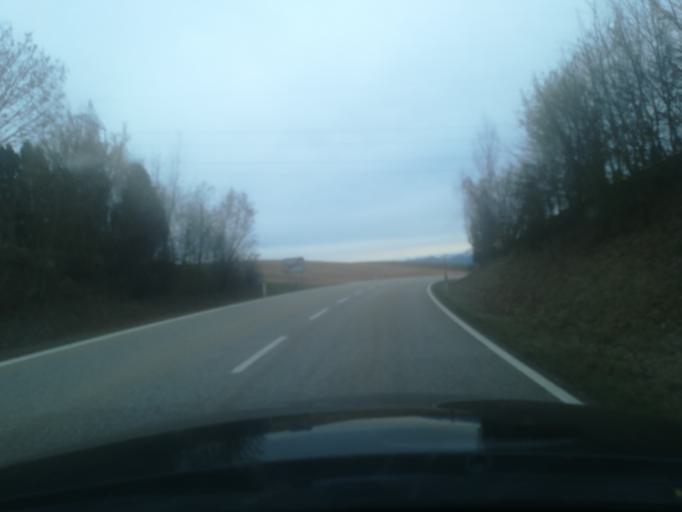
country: AT
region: Upper Austria
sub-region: Wels-Land
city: Neukirchen bei Lambach
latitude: 48.1036
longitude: 13.8272
